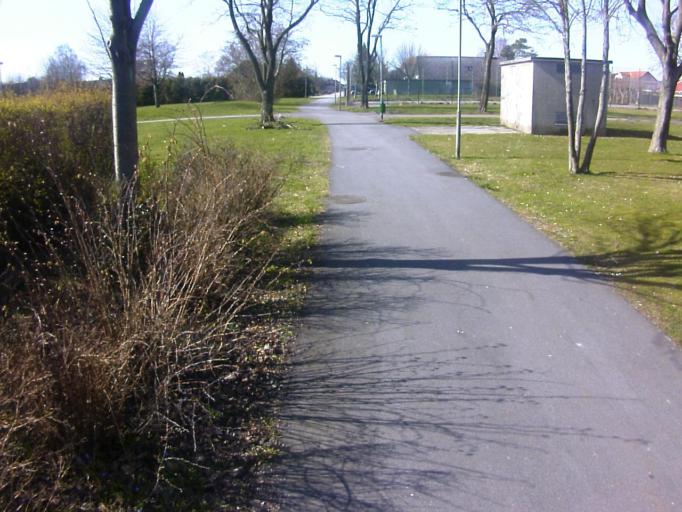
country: SE
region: Skane
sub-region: Kavlinge Kommun
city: Kaevlinge
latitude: 55.7928
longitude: 13.0915
